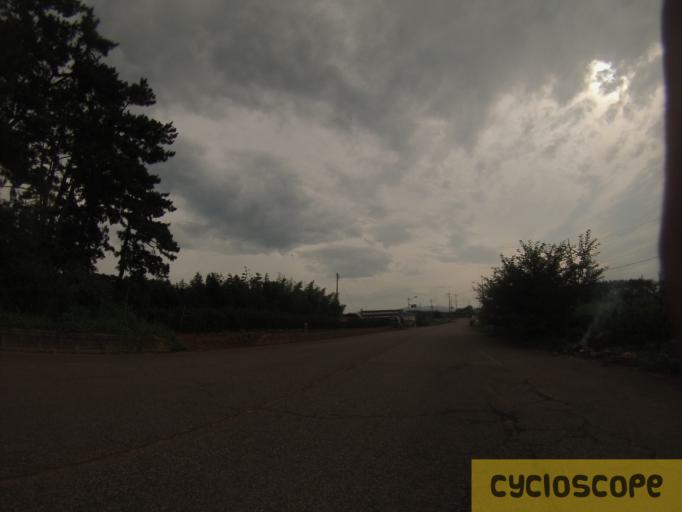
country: KR
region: Jeollabuk-do
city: Kimje
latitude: 35.8477
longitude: 126.8161
